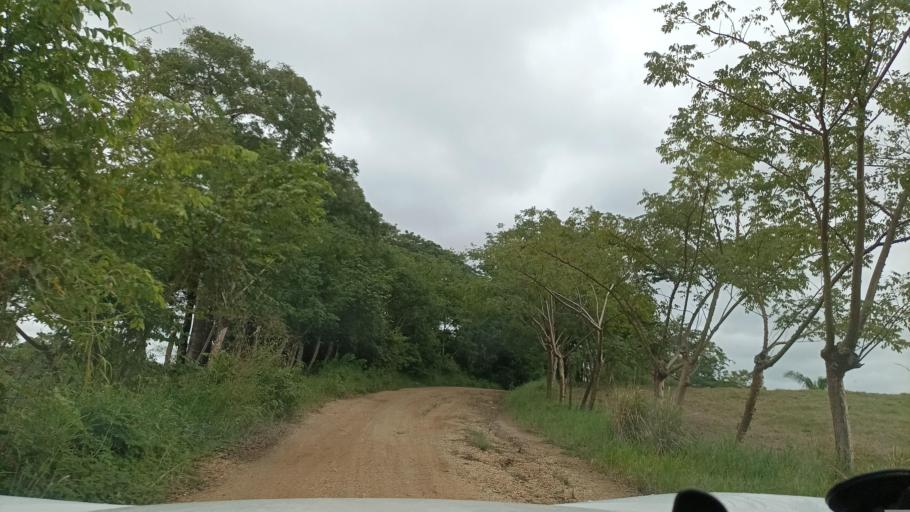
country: MX
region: Veracruz
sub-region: Moloacan
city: Cuichapa
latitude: 17.7928
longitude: -94.3708
